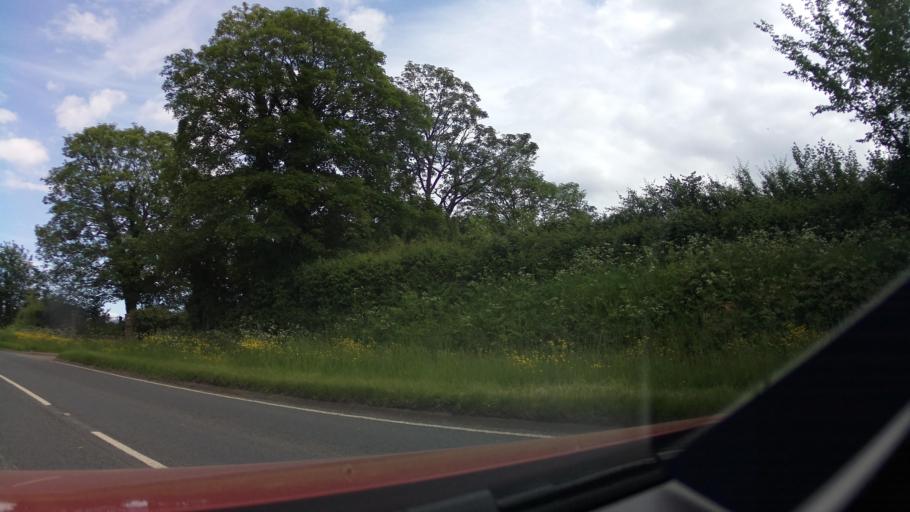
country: GB
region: England
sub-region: Worcestershire
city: Kempsey
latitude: 52.1649
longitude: -2.1729
